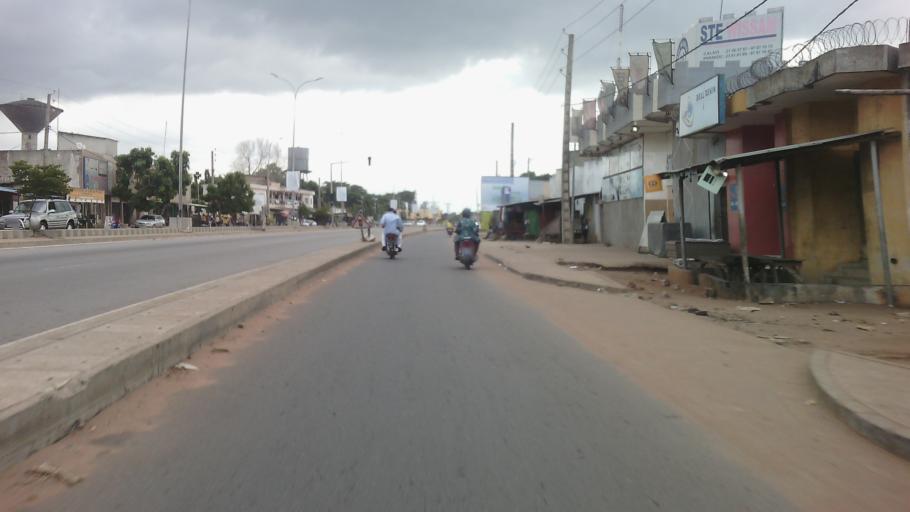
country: BJ
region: Atlantique
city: Abomey-Calavi
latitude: 6.4566
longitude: 2.3568
